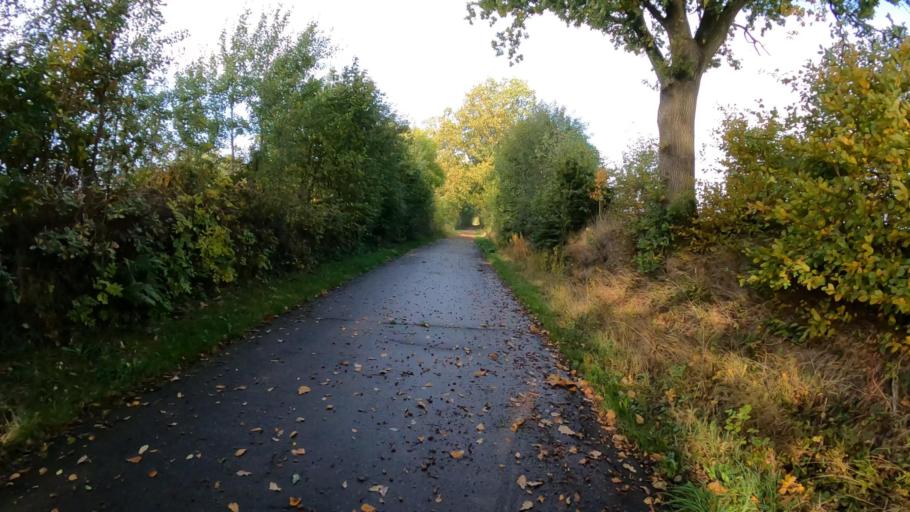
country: DE
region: Schleswig-Holstein
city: Grosshansdorf
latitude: 53.6886
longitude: 10.2729
